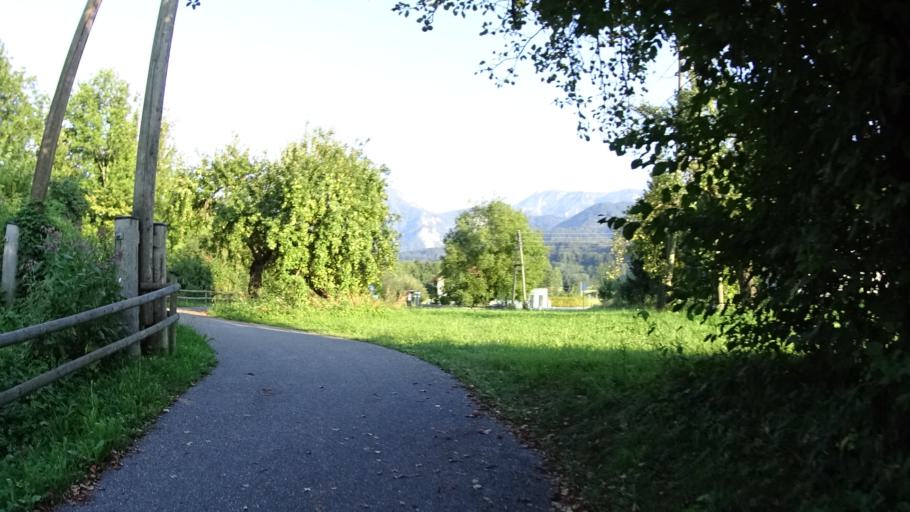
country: AT
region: Carinthia
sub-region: Politischer Bezirk Villach Land
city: Sankt Jakob
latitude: 46.5353
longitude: 14.0876
